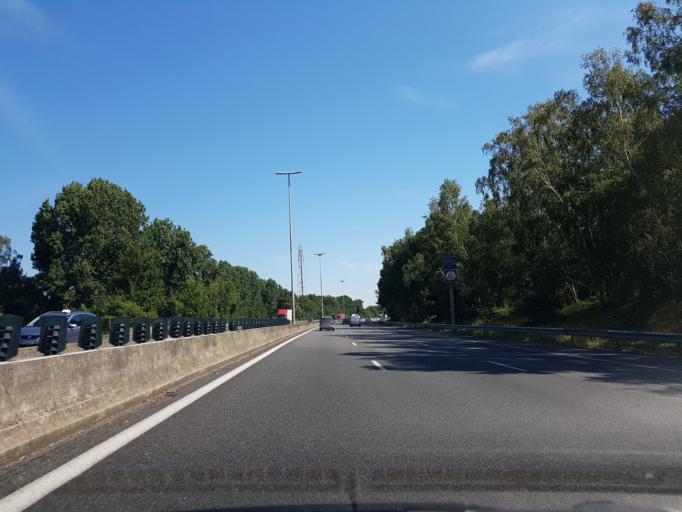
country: FR
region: Picardie
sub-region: Departement de l'Oise
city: La Chapelle-en-Serval
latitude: 49.1265
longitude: 2.5575
